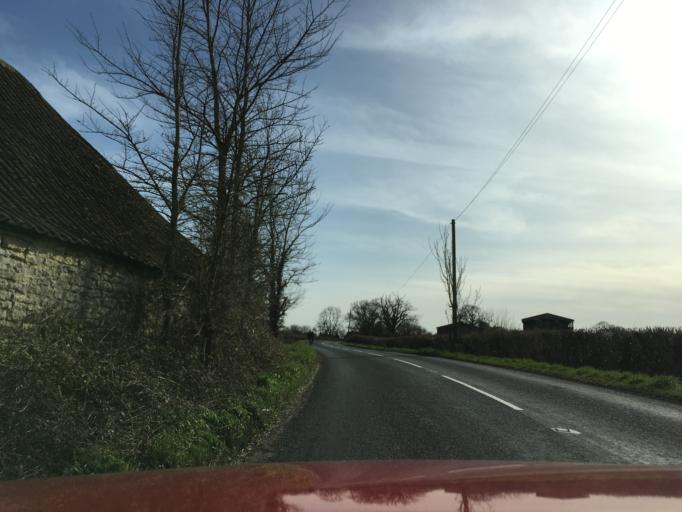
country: GB
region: England
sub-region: Wiltshire
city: Luckington
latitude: 51.5386
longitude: -2.2570
